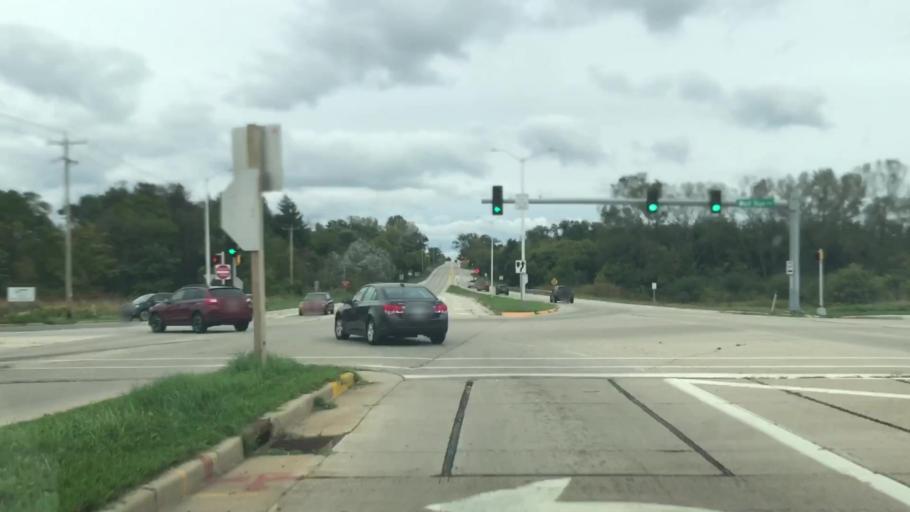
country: US
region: Wisconsin
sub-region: Waukesha County
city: Mukwonago
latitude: 42.8487
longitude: -88.3187
